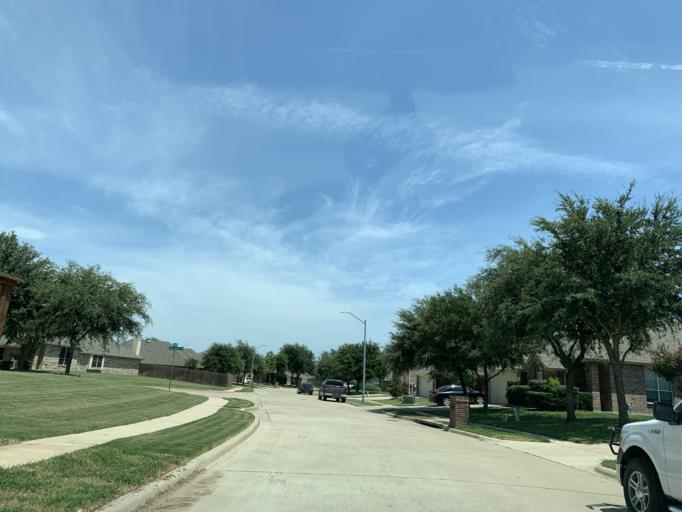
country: US
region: Texas
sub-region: Dallas County
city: Cedar Hill
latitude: 32.6448
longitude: -97.0258
